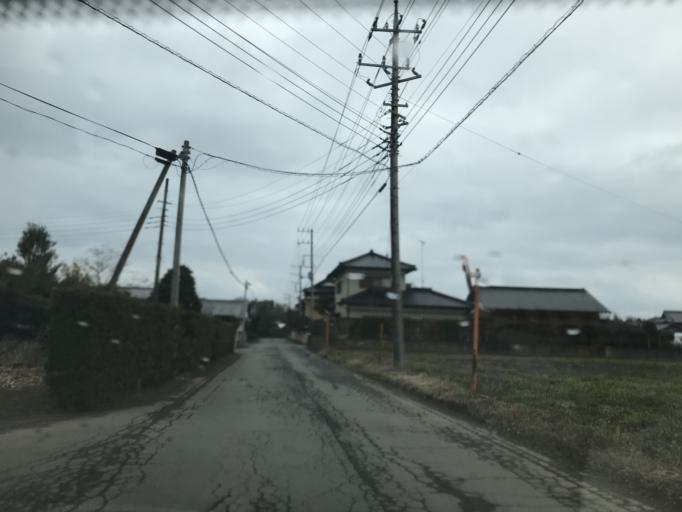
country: JP
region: Chiba
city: Sawara
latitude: 35.8515
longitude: 140.5428
